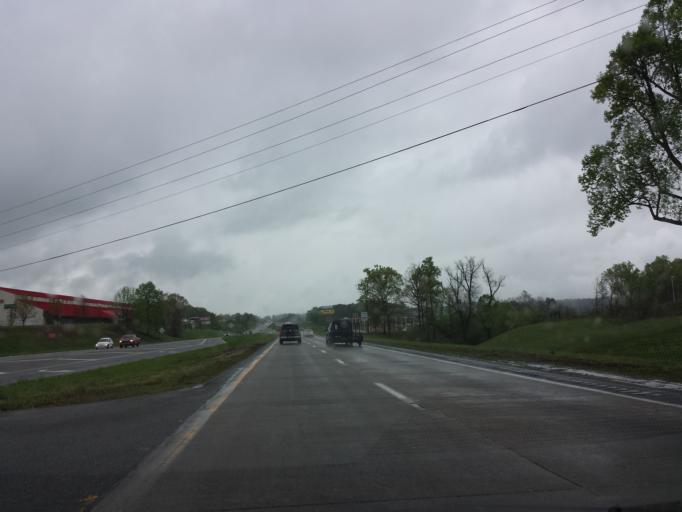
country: US
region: Georgia
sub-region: Pickens County
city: Jasper
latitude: 34.4582
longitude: -84.4547
